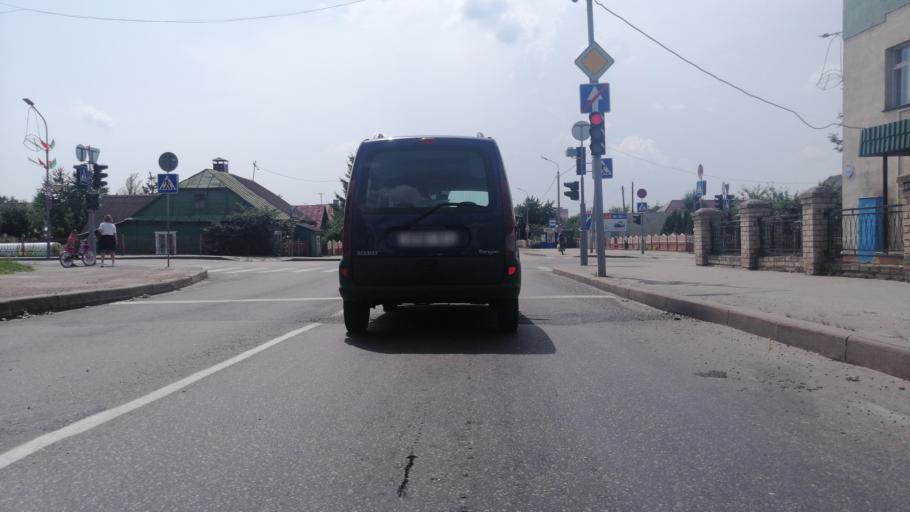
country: BY
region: Grodnenskaya
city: Navahrudak
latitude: 53.5920
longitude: 25.8184
